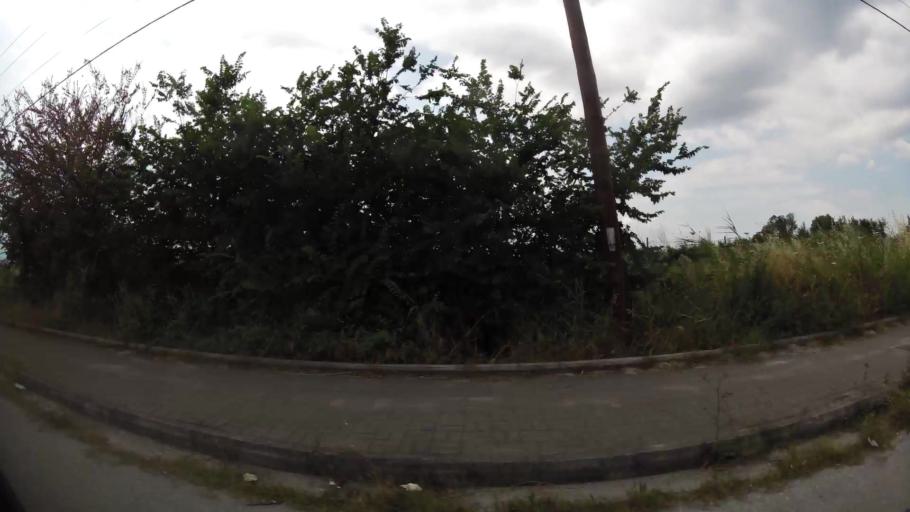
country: GR
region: Central Macedonia
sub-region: Nomos Pierias
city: Paralia
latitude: 40.2712
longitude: 22.5946
